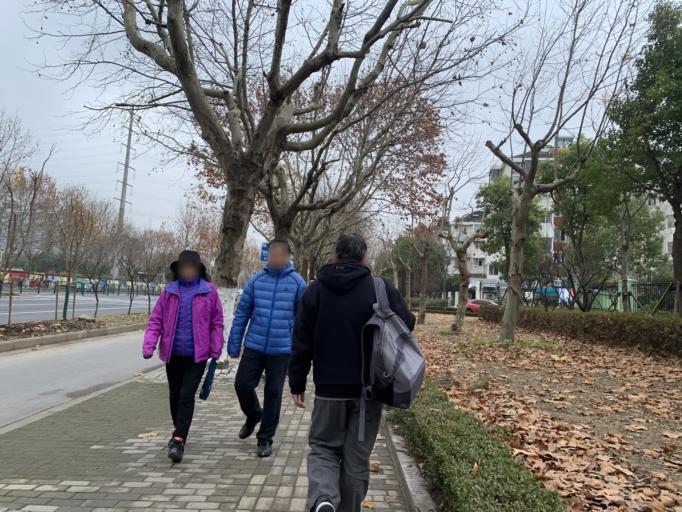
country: CN
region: Shanghai Shi
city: Huamu
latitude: 31.1916
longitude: 121.5352
